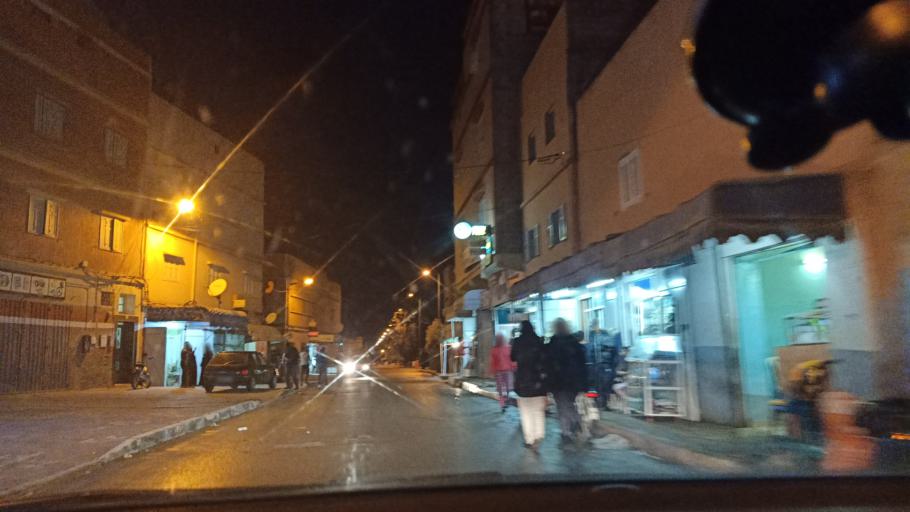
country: MA
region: Doukkala-Abda
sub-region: Safi
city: Youssoufia
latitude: 32.2525
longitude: -8.5346
